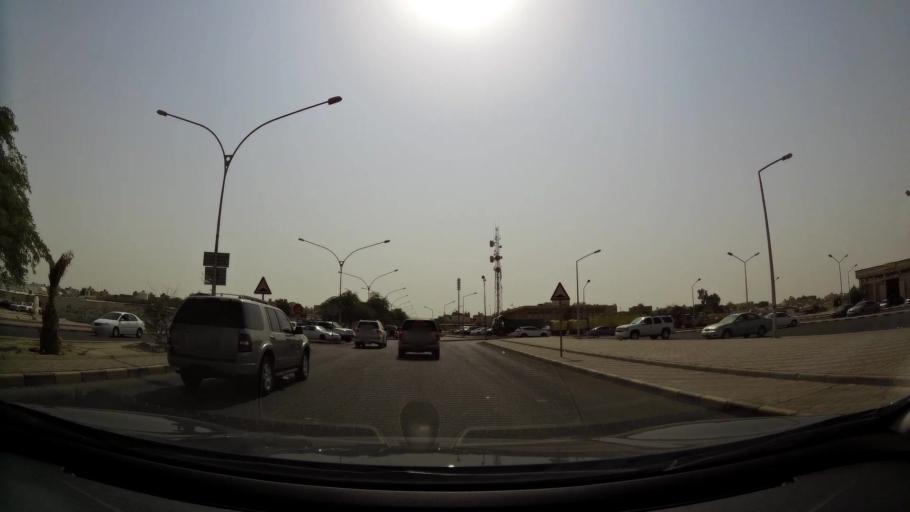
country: KW
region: Muhafazat al Jahra'
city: Al Jahra'
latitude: 29.3274
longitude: 47.6805
